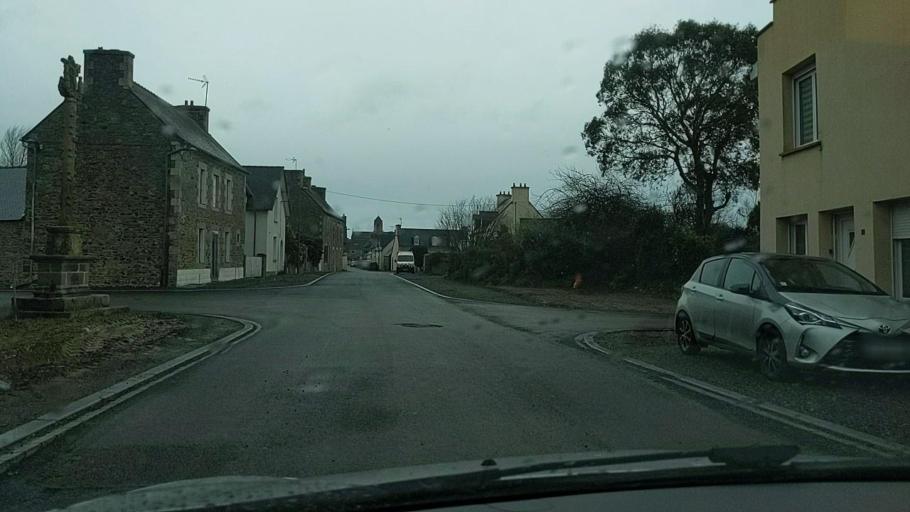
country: FR
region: Brittany
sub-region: Departement des Cotes-d'Armor
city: Pleumeur-Gautier
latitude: 48.7999
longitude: -3.1568
